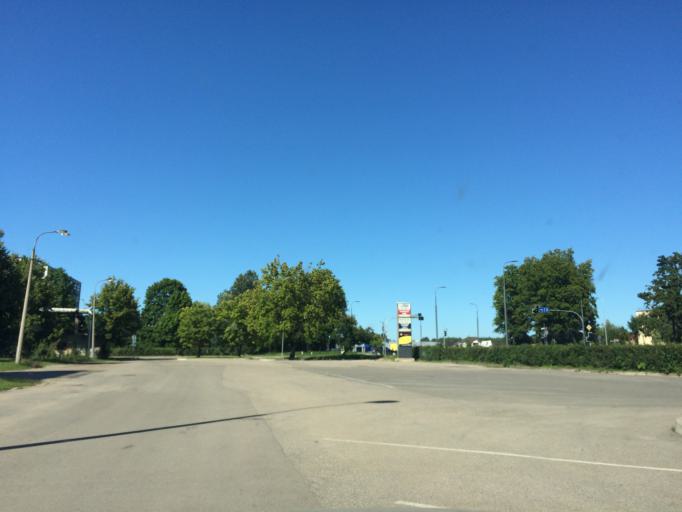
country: LV
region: Rezekne
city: Rezekne
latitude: 56.5286
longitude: 27.3435
